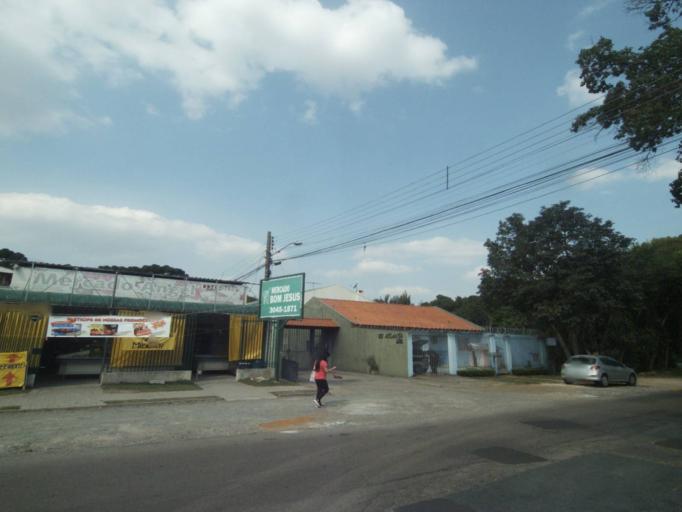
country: BR
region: Parana
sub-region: Sao Jose Dos Pinhais
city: Sao Jose dos Pinhais
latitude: -25.5204
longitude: -49.2433
